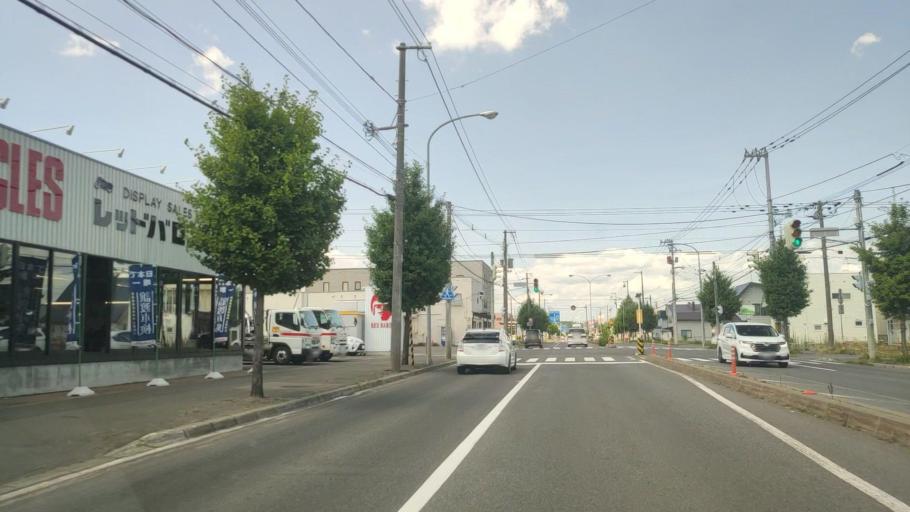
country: JP
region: Hokkaido
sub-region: Asahikawa-shi
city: Asahikawa
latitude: 43.8011
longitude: 142.3918
